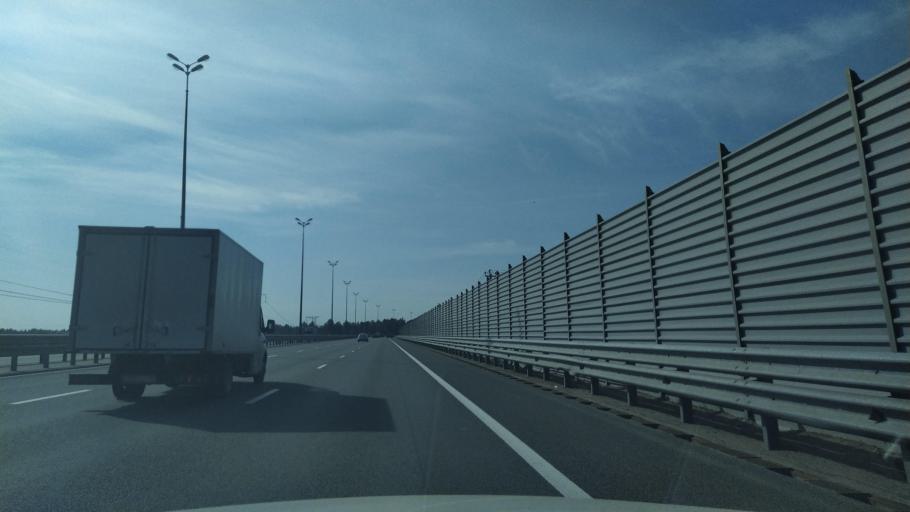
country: RU
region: Leningrad
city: Maloye Verevo
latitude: 59.5891
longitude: 30.1829
